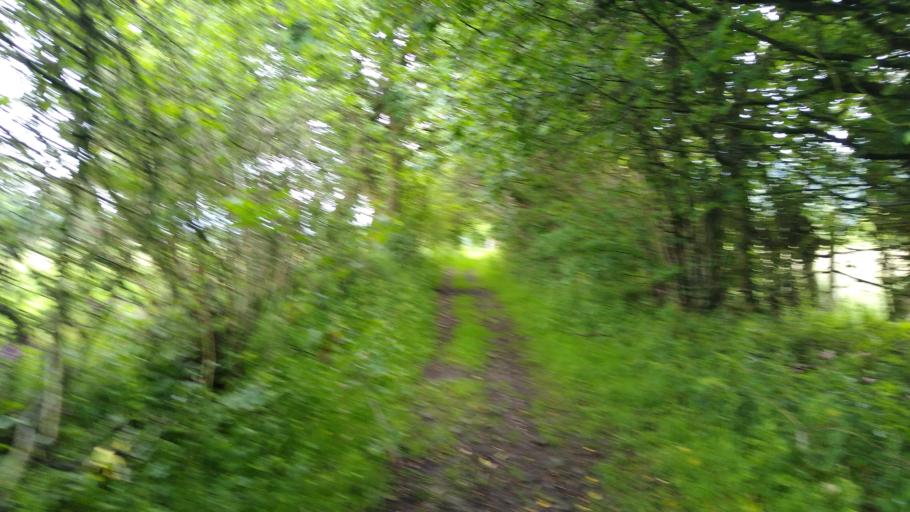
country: GB
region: England
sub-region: Cumbria
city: Cockermouth
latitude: 54.6562
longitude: -3.2803
